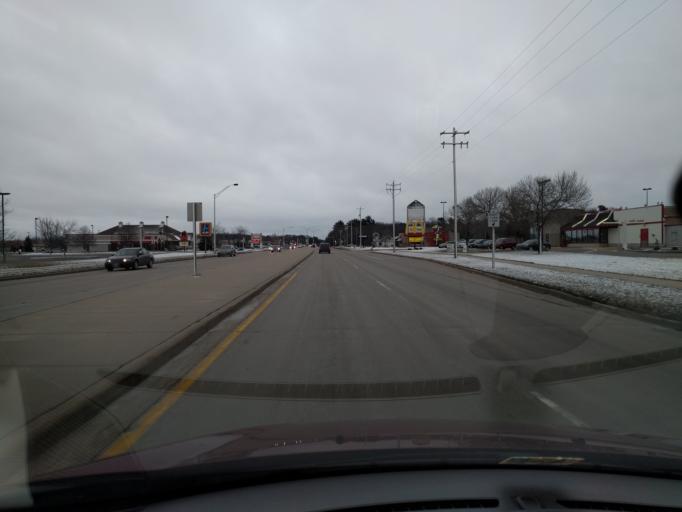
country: US
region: Wisconsin
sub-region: Portage County
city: Whiting
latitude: 44.5234
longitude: -89.5076
